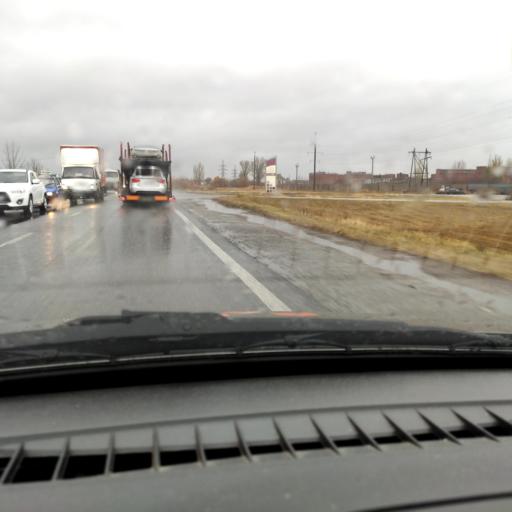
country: RU
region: Samara
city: Tol'yatti
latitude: 53.5690
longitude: 49.3459
